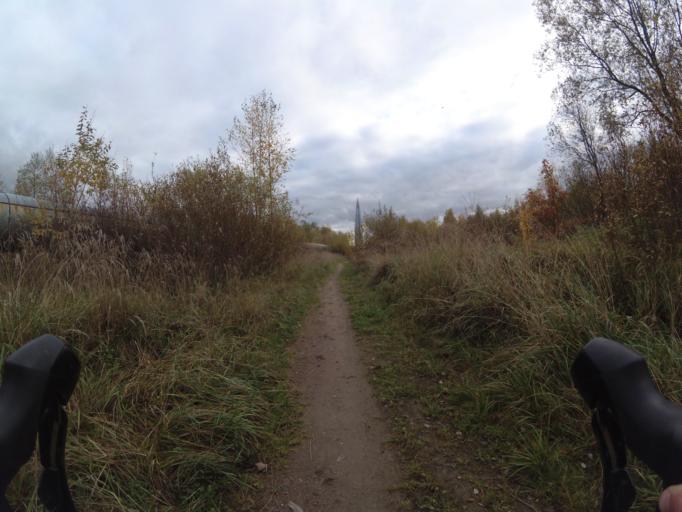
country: RU
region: St.-Petersburg
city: Lakhtinskiy
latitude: 60.0027
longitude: 30.1523
